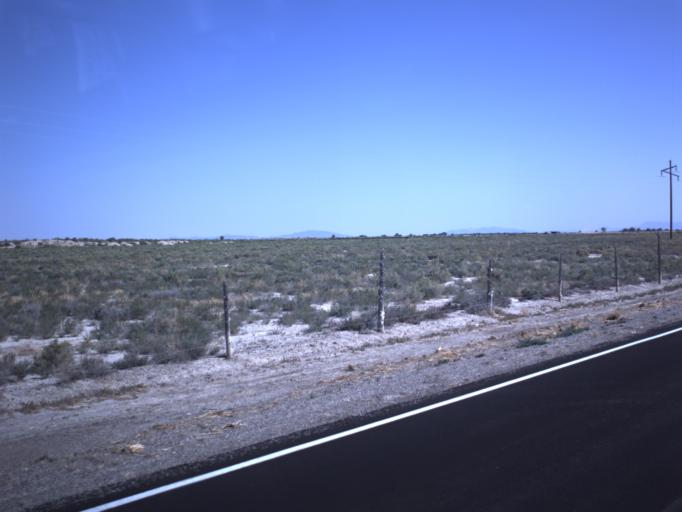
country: US
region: Utah
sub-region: Millard County
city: Delta
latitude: 39.2340
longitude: -112.6669
